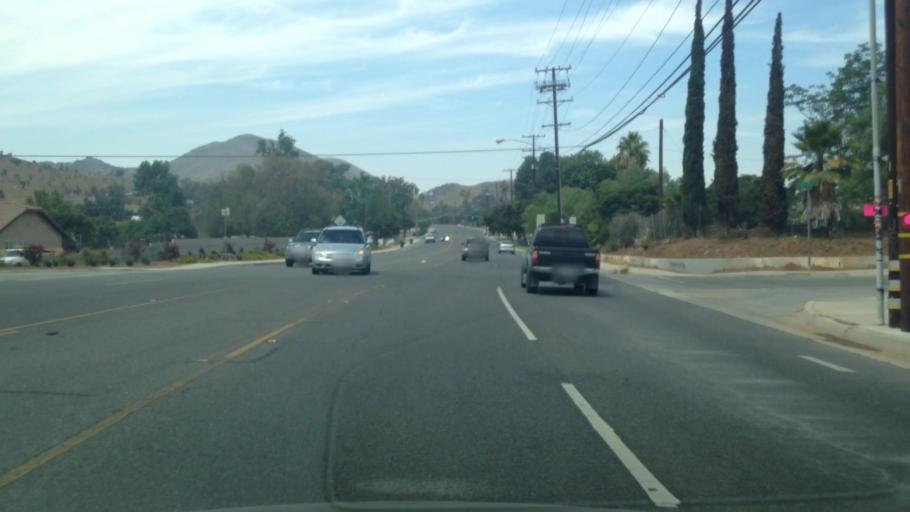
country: US
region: California
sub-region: Riverside County
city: Pedley
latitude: 33.9442
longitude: -117.4885
